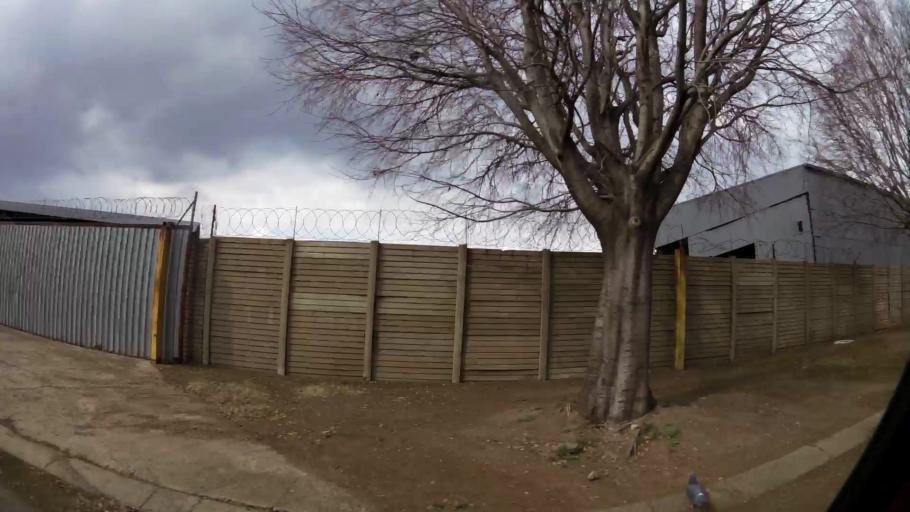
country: ZA
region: Gauteng
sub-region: Sedibeng District Municipality
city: Vanderbijlpark
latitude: -26.6879
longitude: 27.8096
